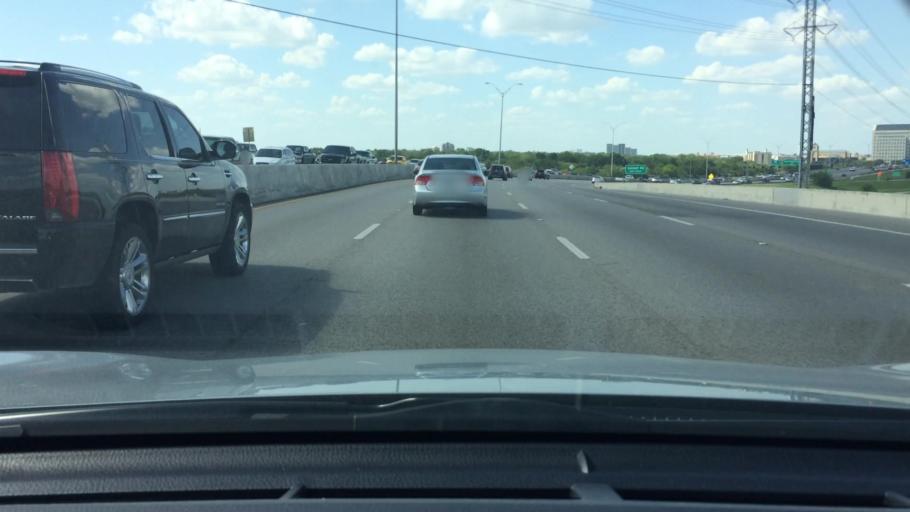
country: US
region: Texas
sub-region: Bexar County
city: Olmos Park
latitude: 29.4948
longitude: -98.4840
